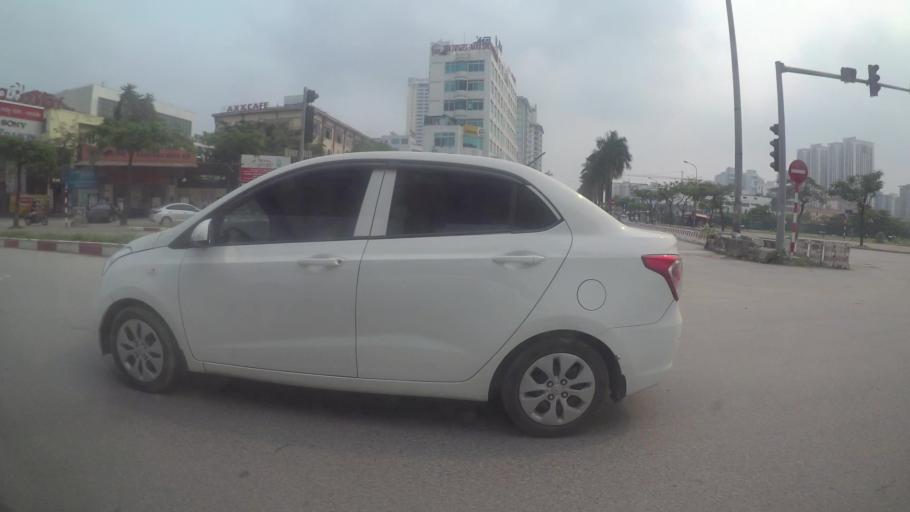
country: VN
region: Ha Noi
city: Cau Dien
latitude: 21.0381
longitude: 105.7722
